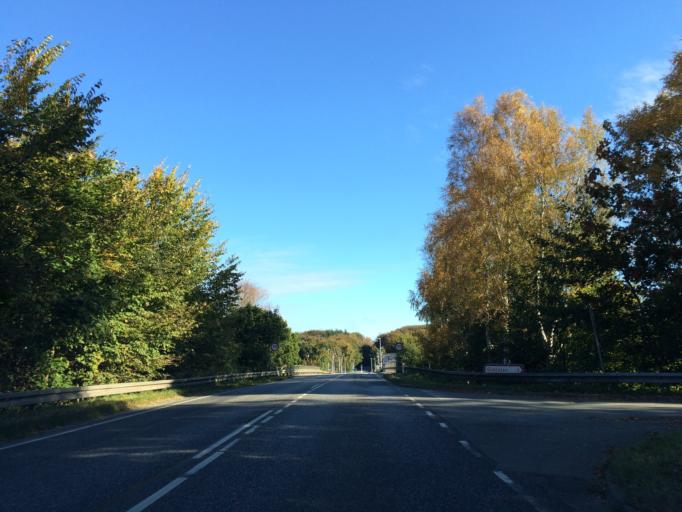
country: DK
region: Central Jutland
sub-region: Randers Kommune
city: Langa
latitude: 56.3578
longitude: 9.9090
